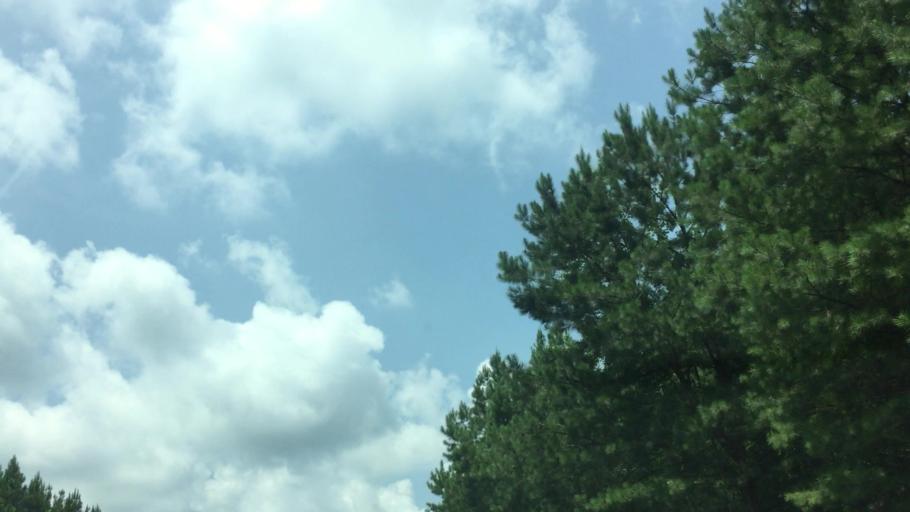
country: US
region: Georgia
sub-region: Fulton County
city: Chattahoochee Hills
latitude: 33.5683
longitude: -84.7211
